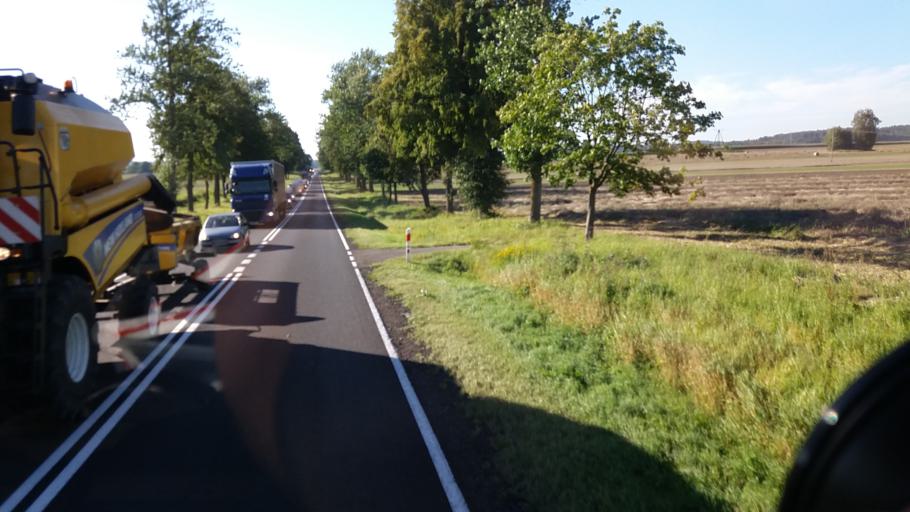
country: PL
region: West Pomeranian Voivodeship
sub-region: Powiat drawski
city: Kalisz Pomorski
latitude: 53.2930
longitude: 15.9351
